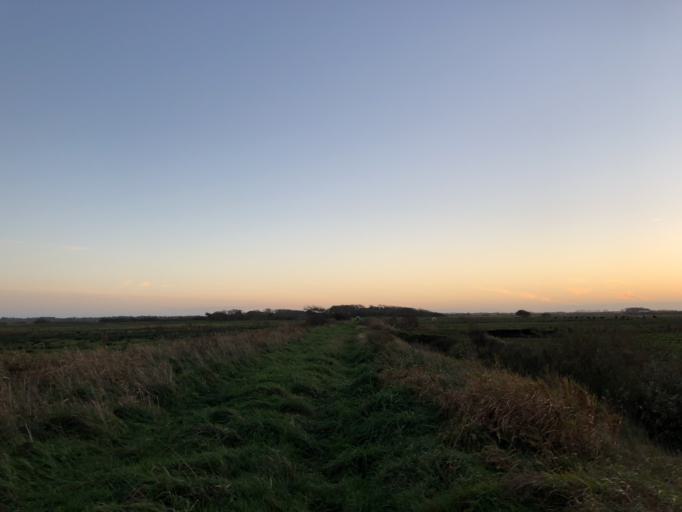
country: DK
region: Central Jutland
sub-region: Holstebro Kommune
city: Ulfborg
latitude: 56.2986
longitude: 8.2976
